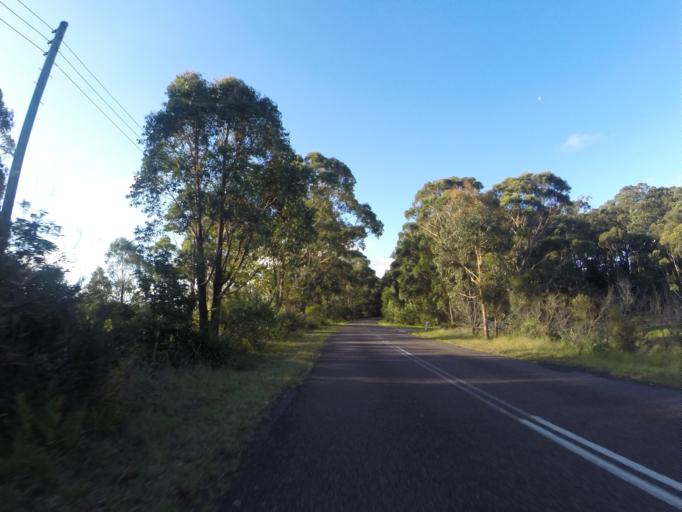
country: AU
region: New South Wales
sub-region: Shoalhaven Shire
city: Kangaroo Valley
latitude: -34.6558
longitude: 150.5027
